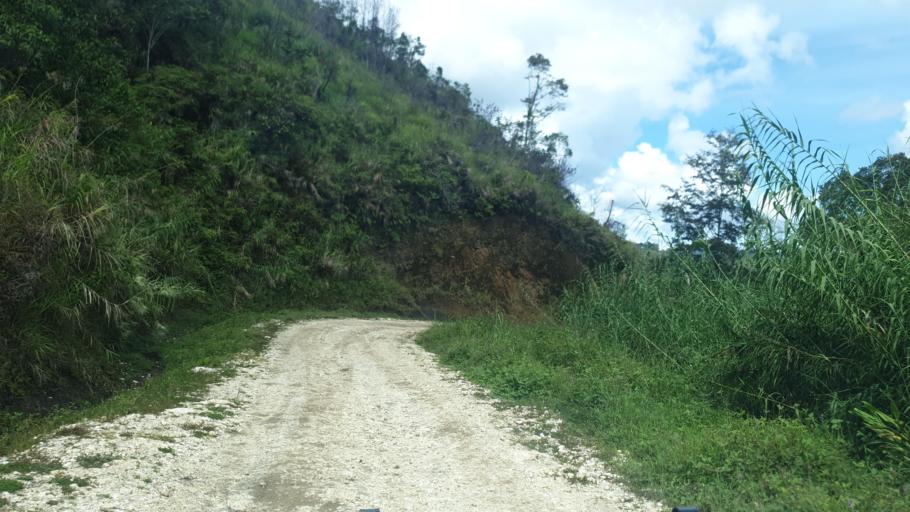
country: PG
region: Chimbu
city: Kundiawa
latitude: -6.2123
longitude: 145.1381
